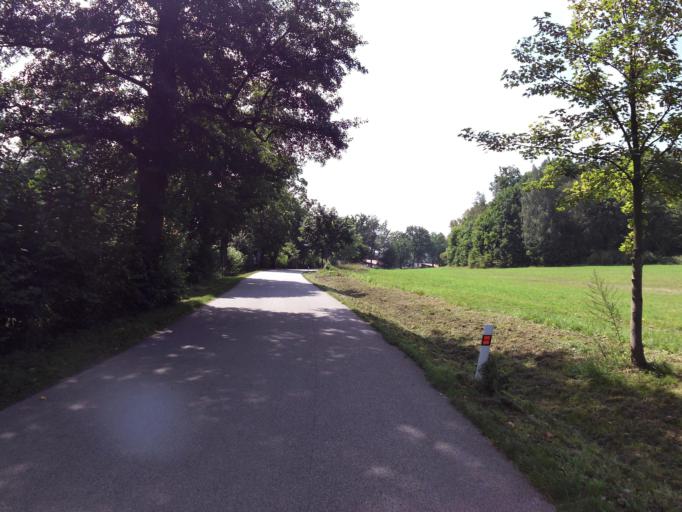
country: CZ
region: Jihocesky
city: Chlum u Trebone
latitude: 48.9652
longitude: 14.9372
